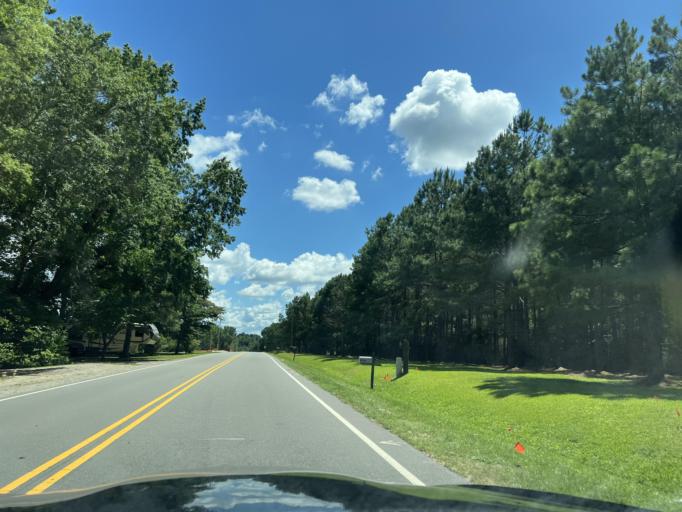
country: US
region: North Carolina
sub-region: Lee County
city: Sanford
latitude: 35.4532
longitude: -79.1697
